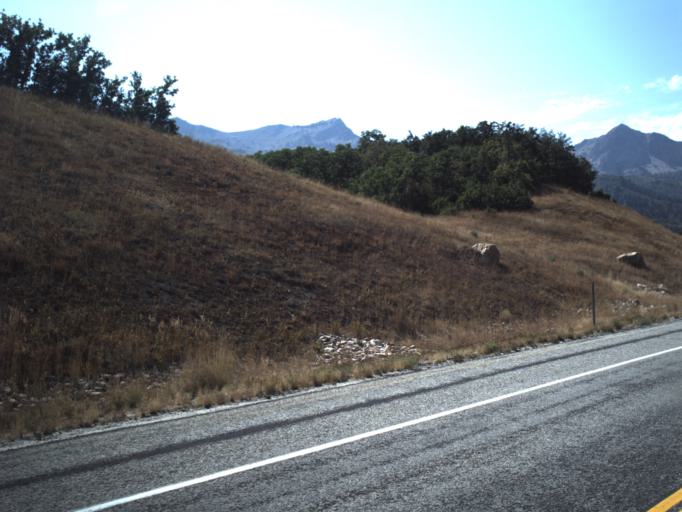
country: US
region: Utah
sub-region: Morgan County
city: Mountain Green
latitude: 41.2056
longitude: -111.8228
